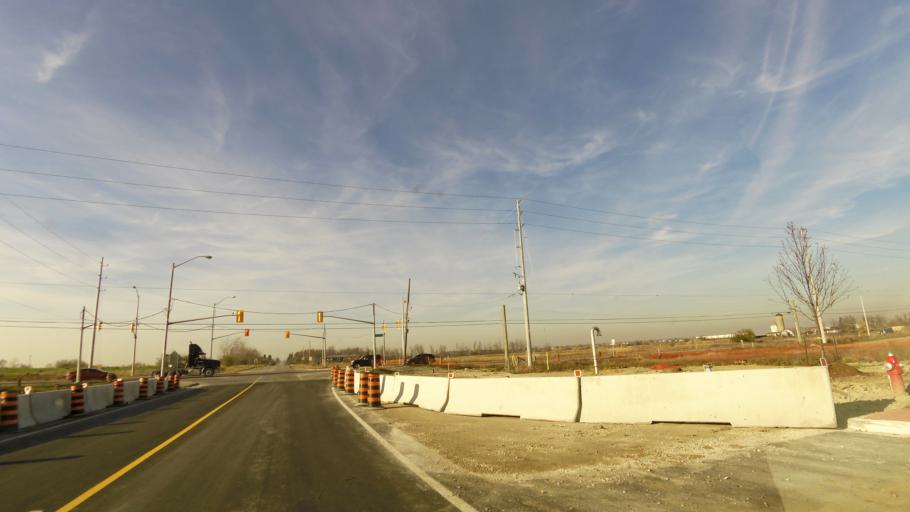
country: CA
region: Ontario
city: Brampton
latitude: 43.7820
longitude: -79.7713
